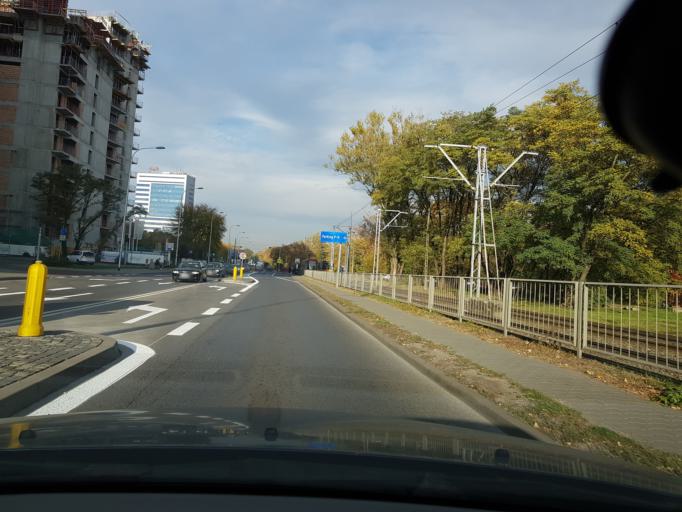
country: PL
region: Masovian Voivodeship
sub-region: Warszawa
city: Bielany
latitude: 52.2816
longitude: 20.9224
